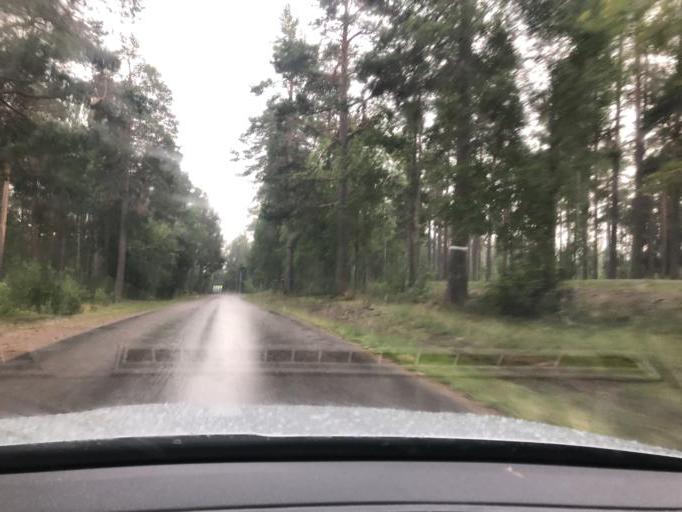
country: SE
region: Vaesternorrland
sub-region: Sundsvalls Kommun
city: Sundsvall
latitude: 62.4018
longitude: 17.3081
